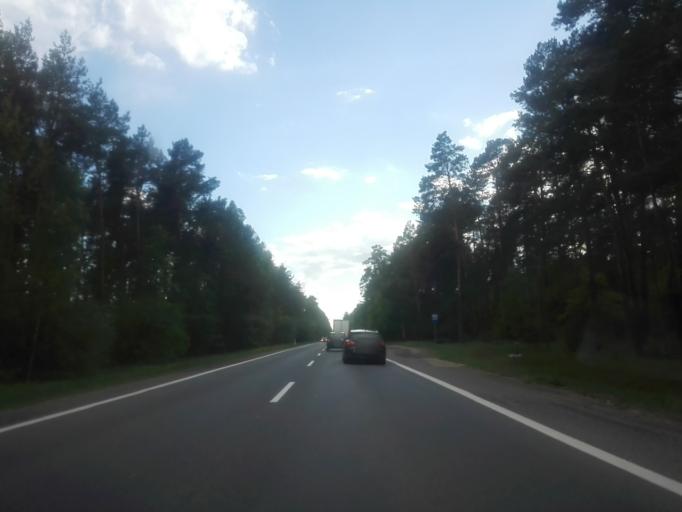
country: PL
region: Masovian Voivodeship
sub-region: Powiat wyszkowski
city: Dlugosiodlo
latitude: 52.6996
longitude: 21.6649
